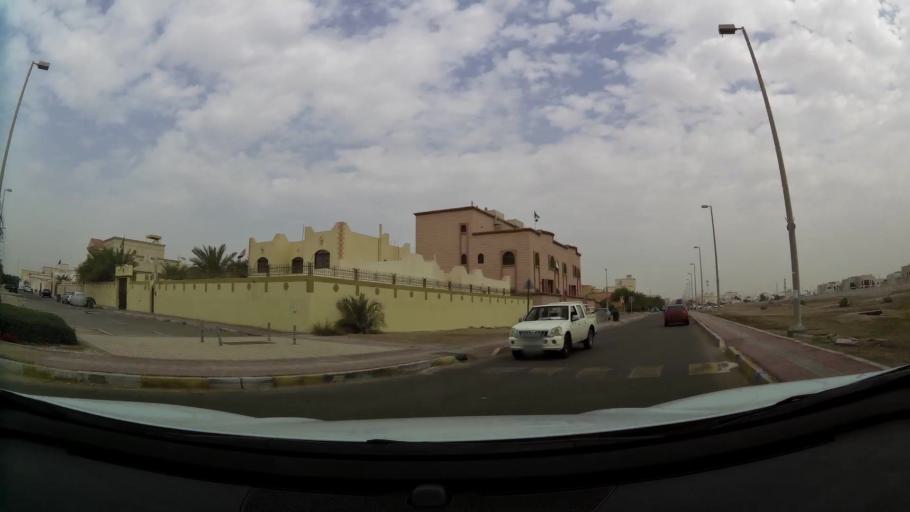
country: AE
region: Abu Dhabi
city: Abu Dhabi
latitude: 24.3160
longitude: 54.6165
